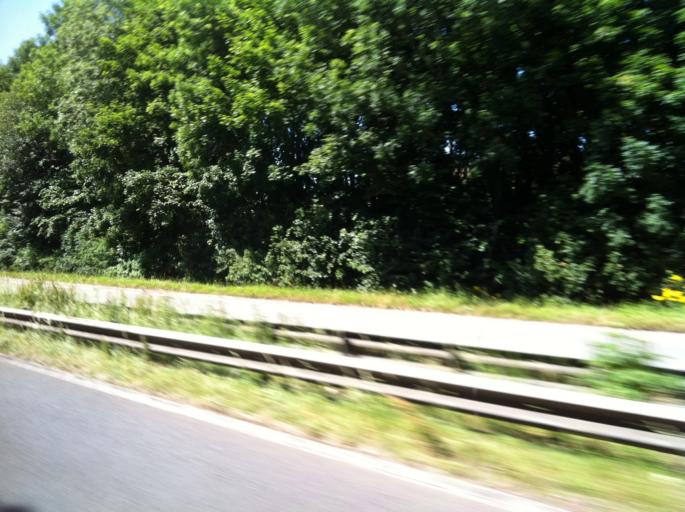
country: GB
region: Wales
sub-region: Cardiff
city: Radyr
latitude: 51.4657
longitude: -3.2583
